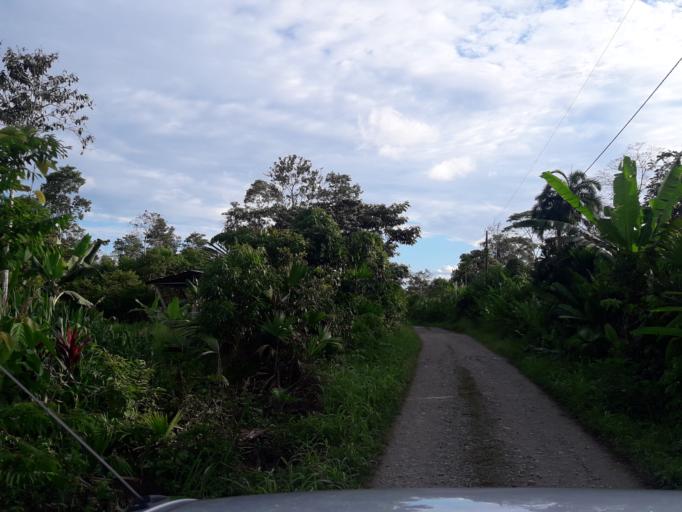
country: EC
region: Orellana
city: Boca Suno
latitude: -0.9008
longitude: -77.3101
